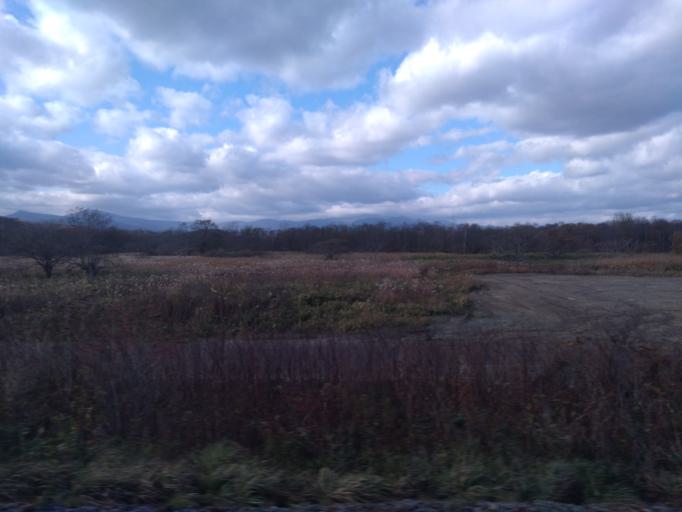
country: JP
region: Hokkaido
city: Shiraoi
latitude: 42.5029
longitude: 141.2765
